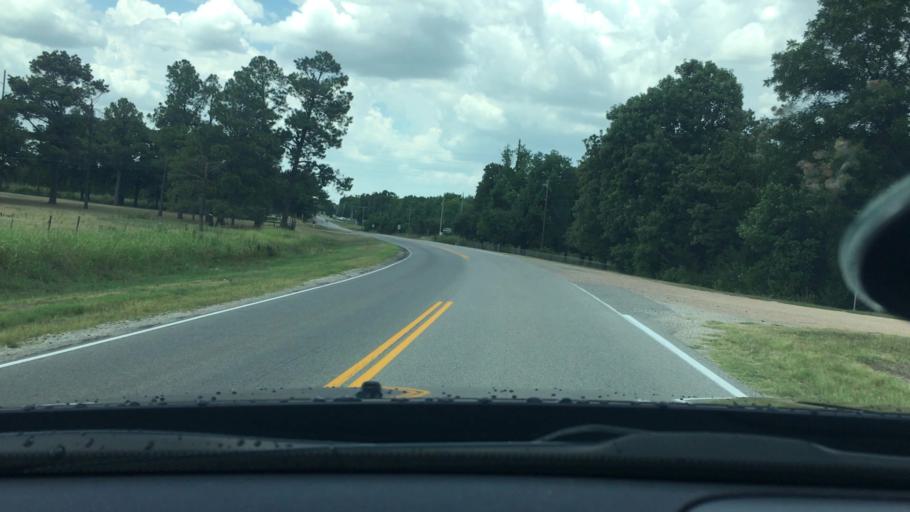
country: US
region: Oklahoma
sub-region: Johnston County
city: Tishomingo
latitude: 34.2289
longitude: -96.6974
